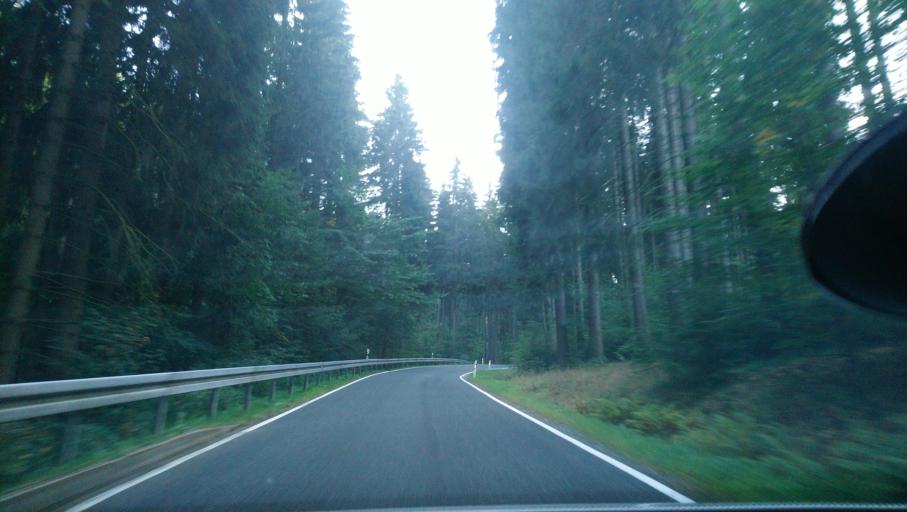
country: DE
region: Saxony
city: Barenstein
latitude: 50.5214
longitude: 13.0466
